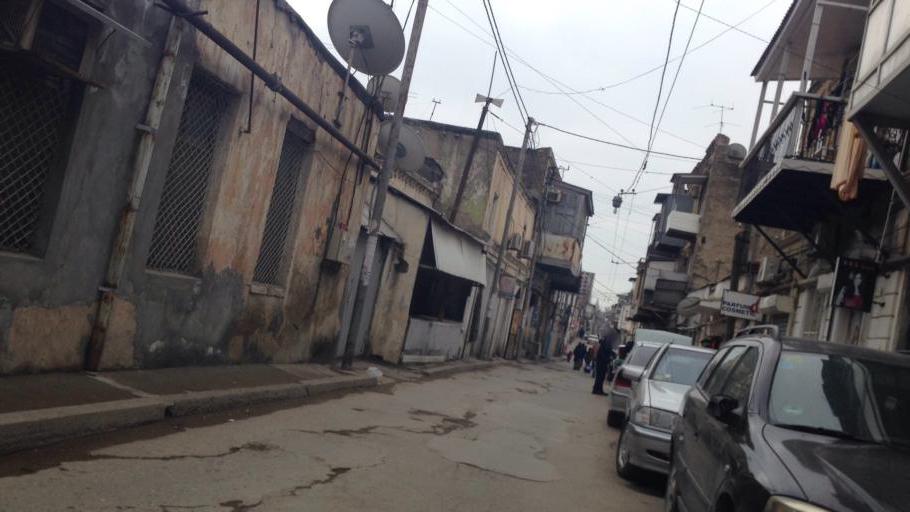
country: AZ
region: Baki
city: Badamdar
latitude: 40.3782
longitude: 49.8293
